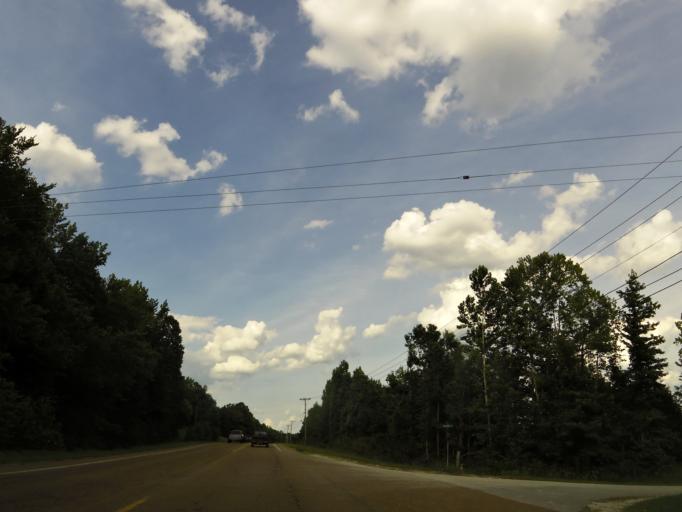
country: US
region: Tennessee
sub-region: Carroll County
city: Bruceton
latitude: 36.0423
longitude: -88.1802
